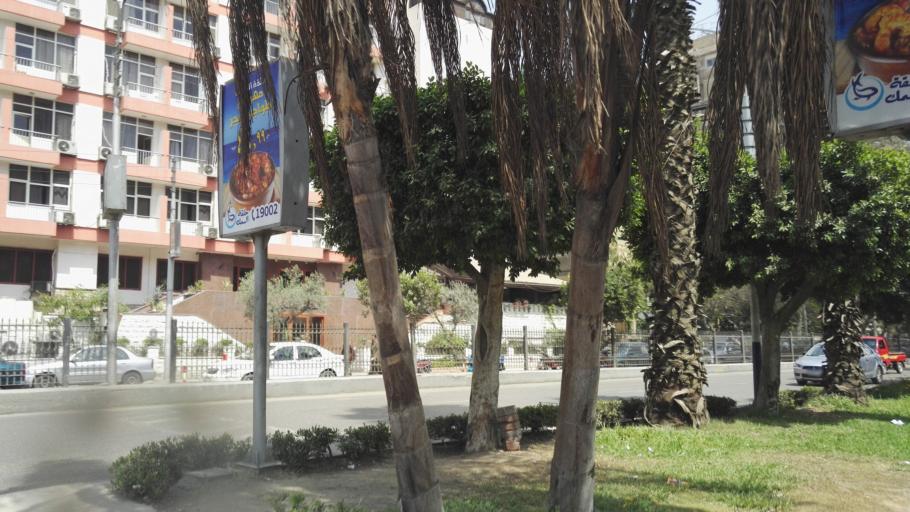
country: EG
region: Muhafazat al Qahirah
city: Cairo
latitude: 30.0846
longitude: 31.3388
